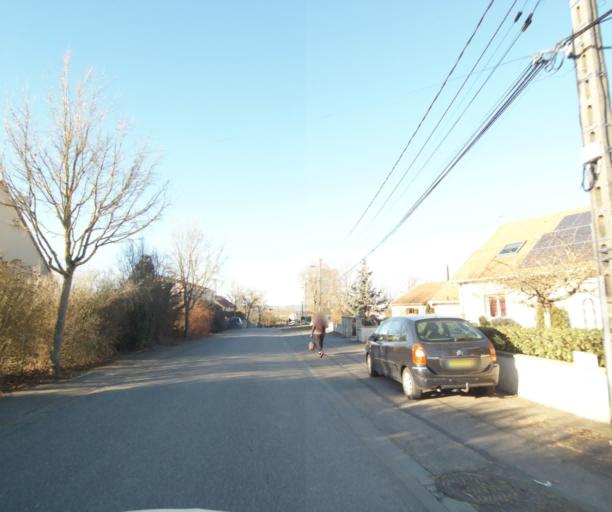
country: FR
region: Lorraine
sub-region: Departement de Meurthe-et-Moselle
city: Laneuveville-devant-Nancy
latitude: 48.6466
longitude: 6.2333
